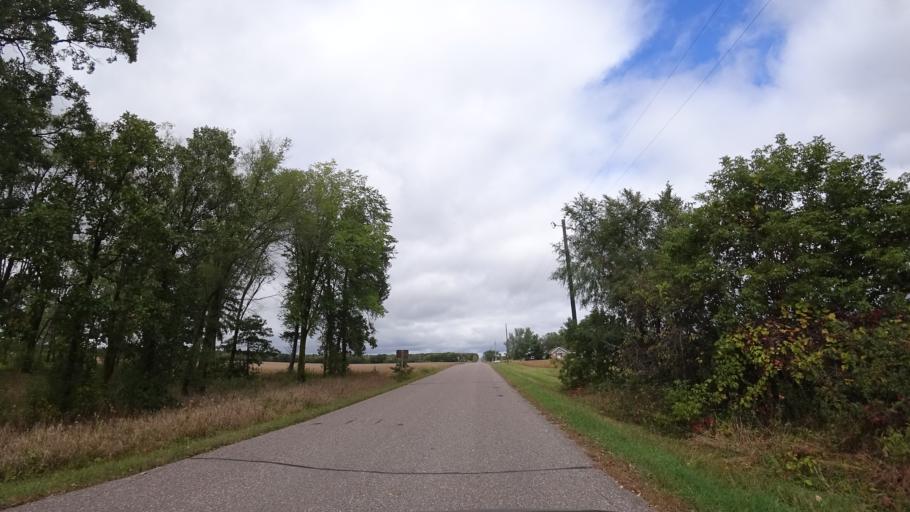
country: US
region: Wisconsin
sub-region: Chippewa County
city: Lake Wissota
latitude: 44.9810
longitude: -91.2869
